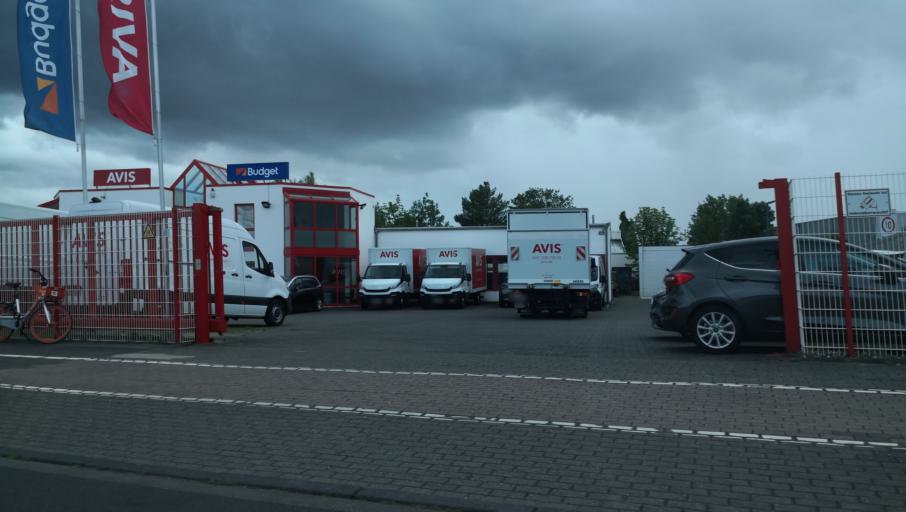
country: DE
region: North Rhine-Westphalia
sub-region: Regierungsbezirk Koln
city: Mengenich
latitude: 50.9829
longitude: 6.8868
